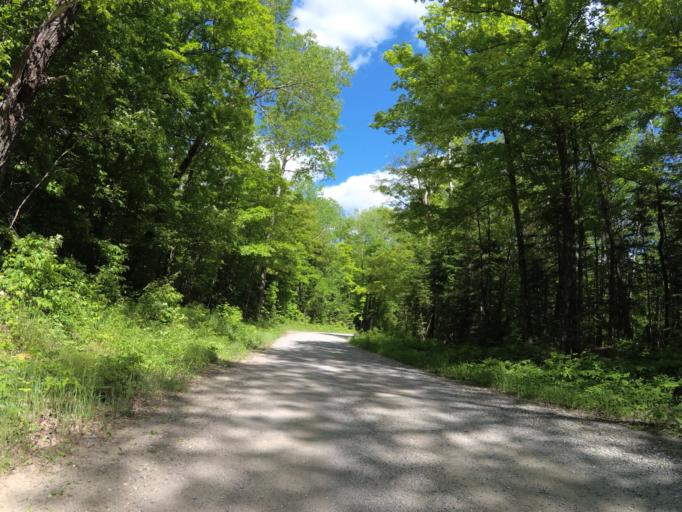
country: CA
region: Ontario
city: Renfrew
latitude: 45.0442
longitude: -76.8260
